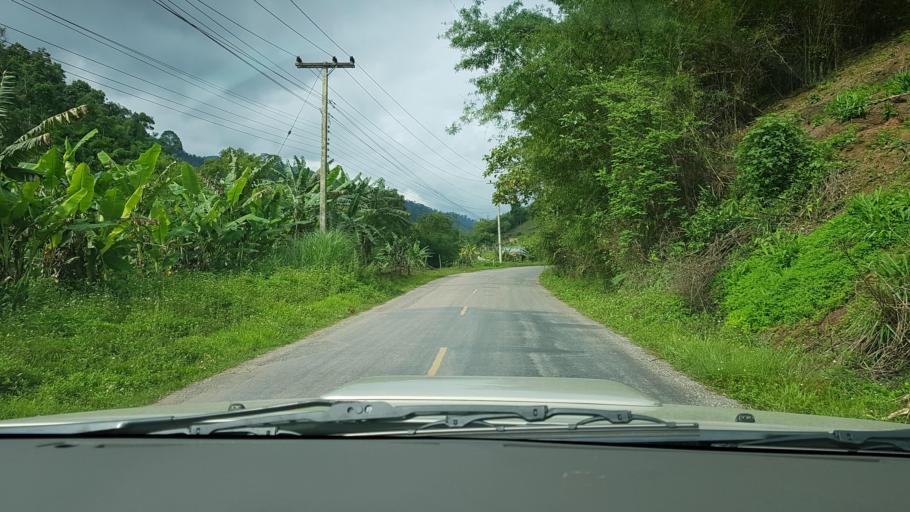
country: LA
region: Oudomxai
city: Muang Xay
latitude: 20.5671
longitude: 101.9204
